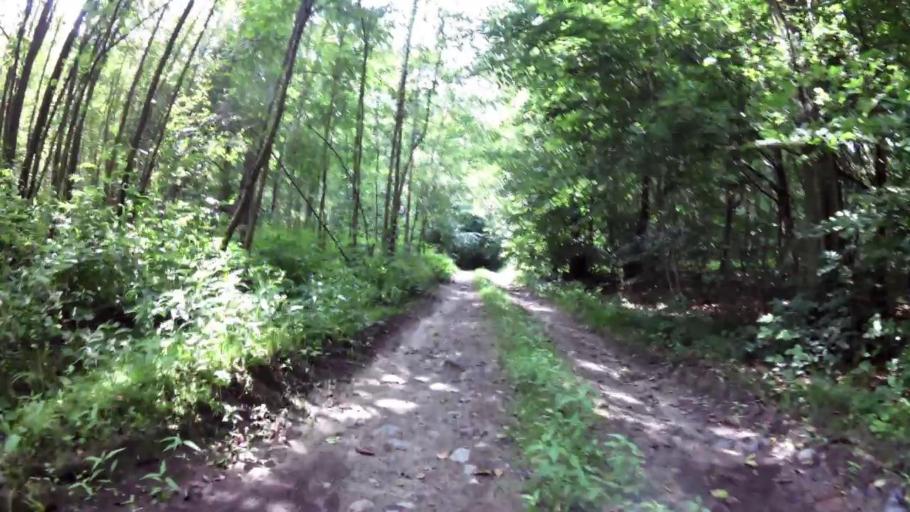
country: PL
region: West Pomeranian Voivodeship
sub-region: Powiat lobeski
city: Wegorzyno
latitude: 53.5142
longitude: 15.6780
